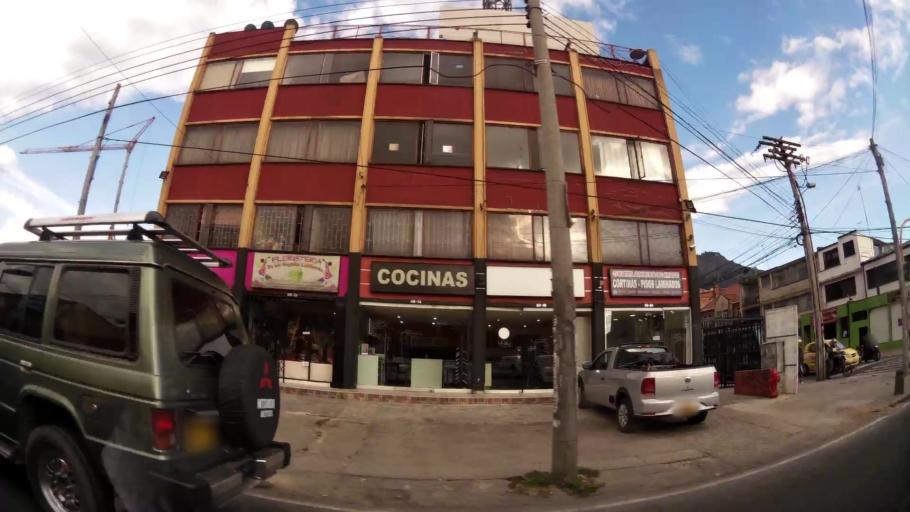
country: CO
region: Bogota D.C.
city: Bogota
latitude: 4.6479
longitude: -74.0681
